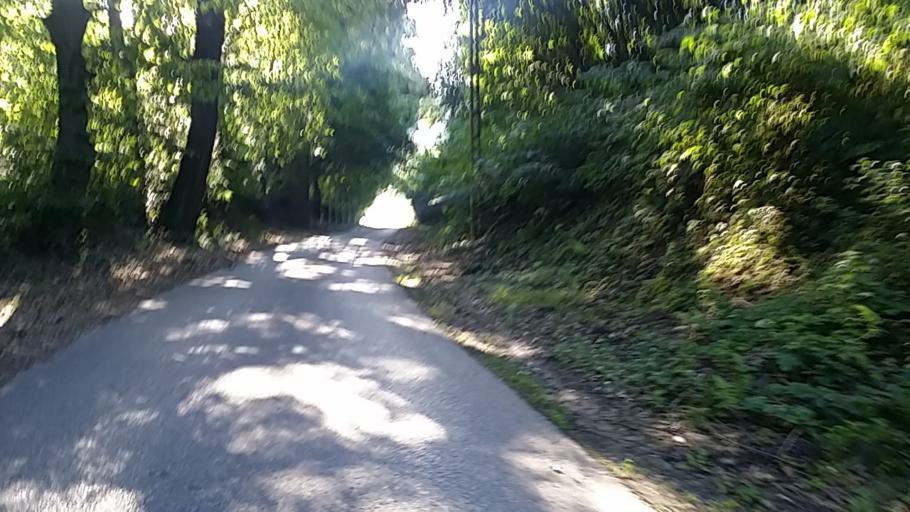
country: HU
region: Baranya
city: Pellerd
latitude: 46.1383
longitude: 18.1136
